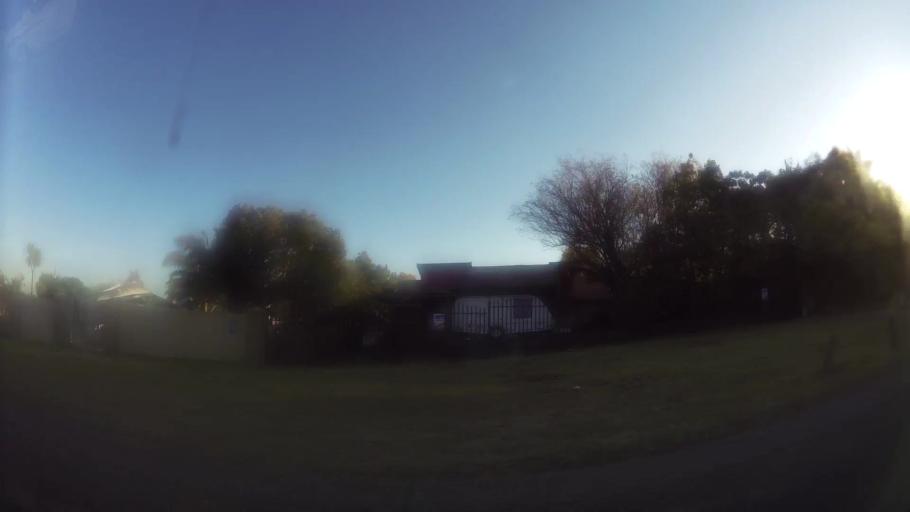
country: ZA
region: Gauteng
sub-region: City of Tshwane Metropolitan Municipality
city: Centurion
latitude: -25.8934
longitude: 28.1370
